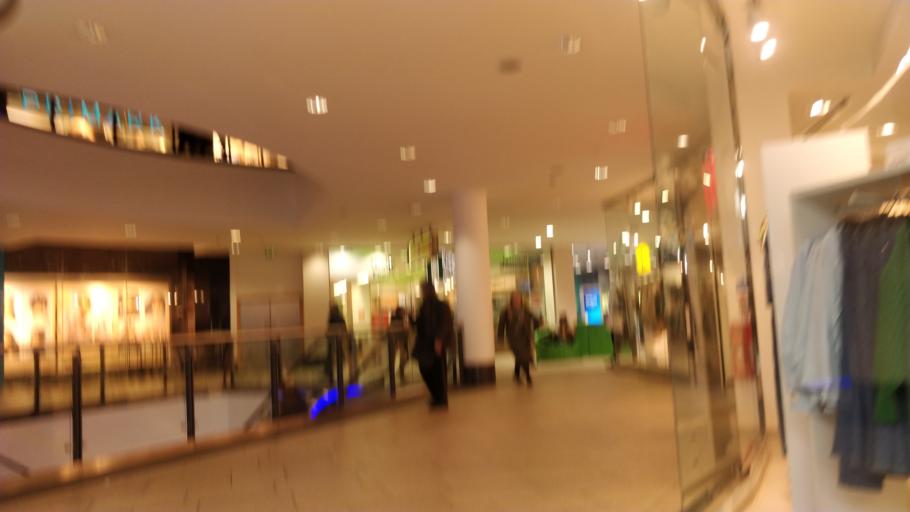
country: GB
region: England
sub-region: City and Borough of Leeds
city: Leeds
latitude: 53.7967
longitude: -1.5454
